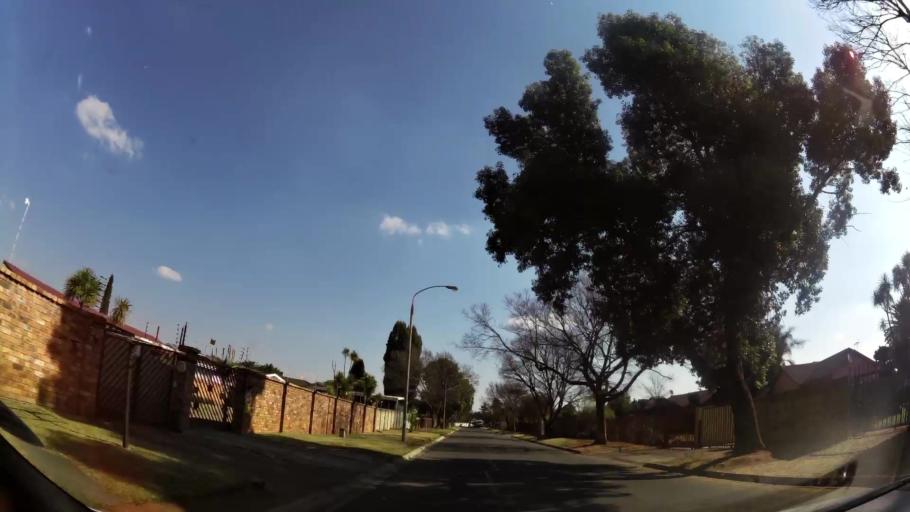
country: ZA
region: Gauteng
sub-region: Ekurhuleni Metropolitan Municipality
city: Boksburg
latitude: -26.2487
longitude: 28.2991
